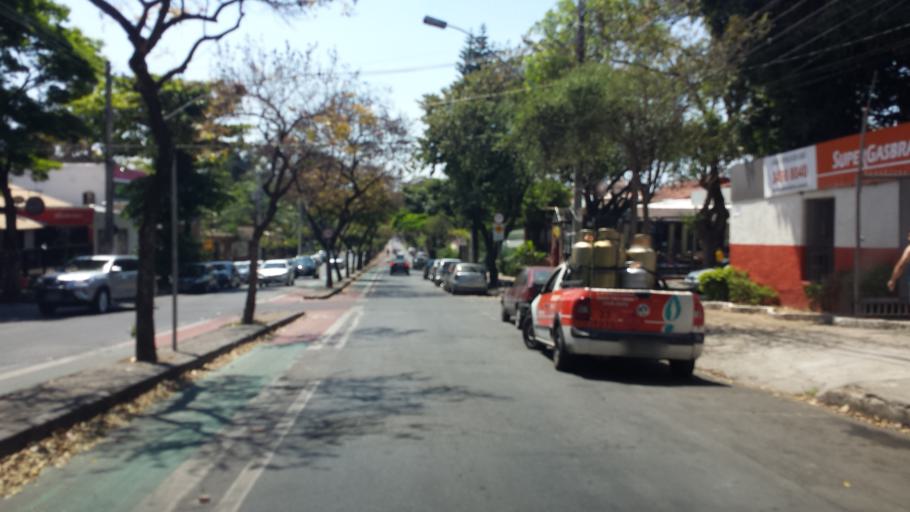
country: BR
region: Minas Gerais
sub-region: Belo Horizonte
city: Belo Horizonte
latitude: -19.8727
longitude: -43.9872
